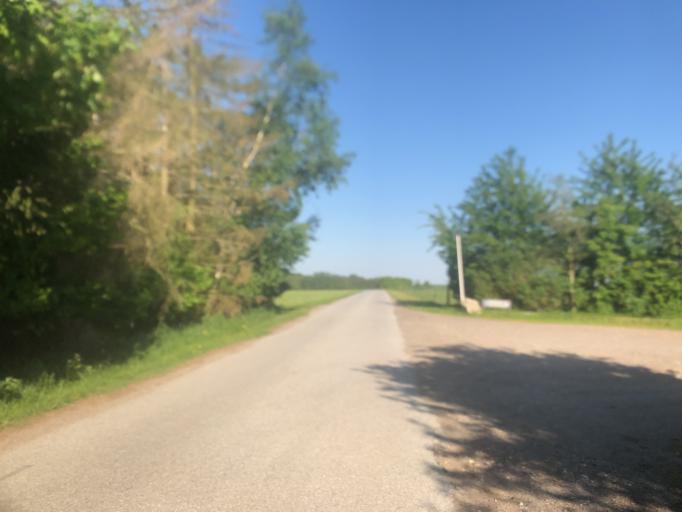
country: DK
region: Zealand
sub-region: Ringsted Kommune
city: Ringsted
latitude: 55.4816
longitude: 11.7773
